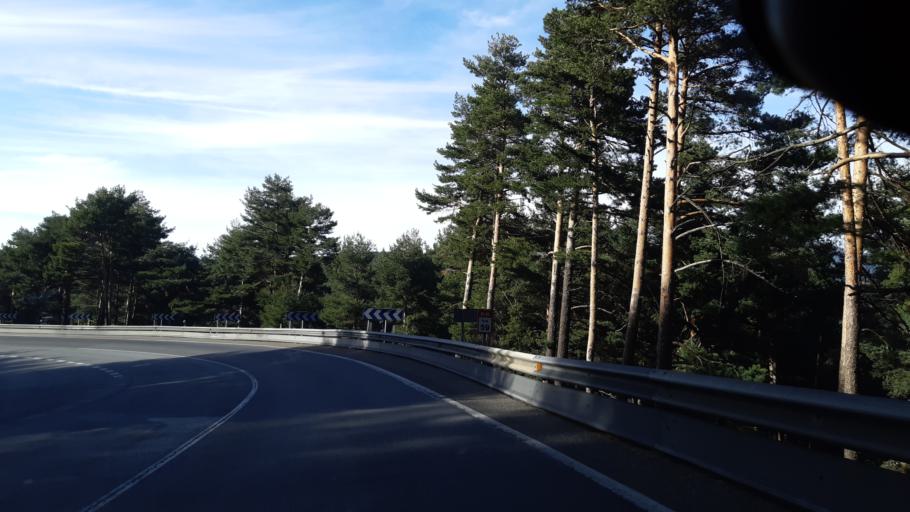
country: ES
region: Madrid
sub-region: Provincia de Madrid
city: Guadarrama
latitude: 40.7101
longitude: -4.1570
